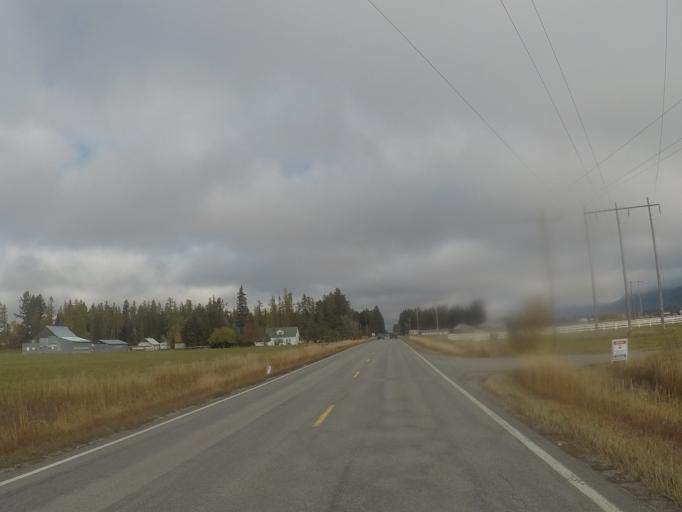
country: US
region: Montana
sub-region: Flathead County
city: Columbia Falls
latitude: 48.3075
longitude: -114.1594
